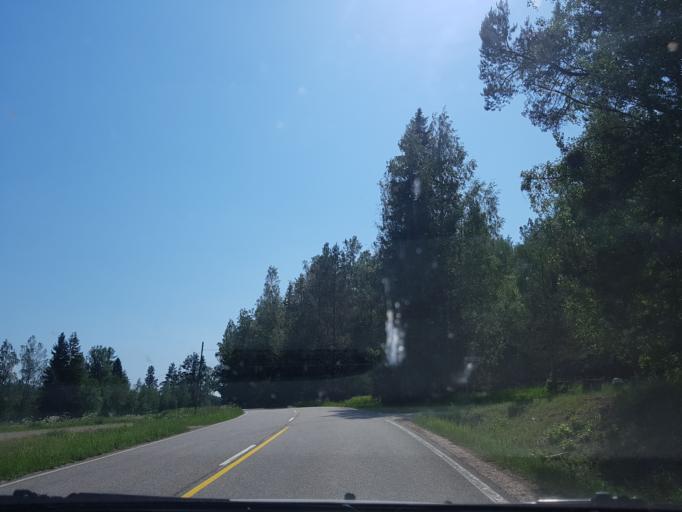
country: FI
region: Uusimaa
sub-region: Helsinki
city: Vihti
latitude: 60.3195
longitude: 24.4031
